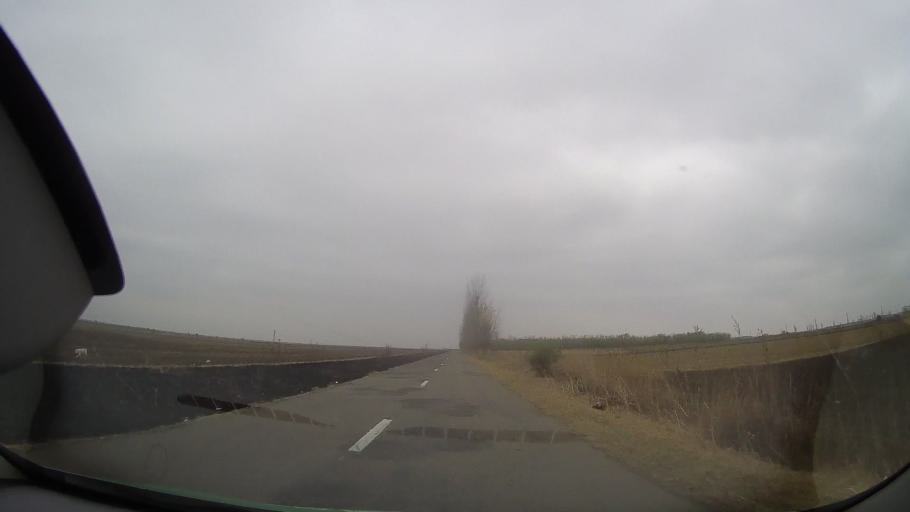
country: RO
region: Ialomita
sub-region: Comuna Valea Macrisului
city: Valea Macrisului
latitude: 44.7424
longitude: 26.8650
